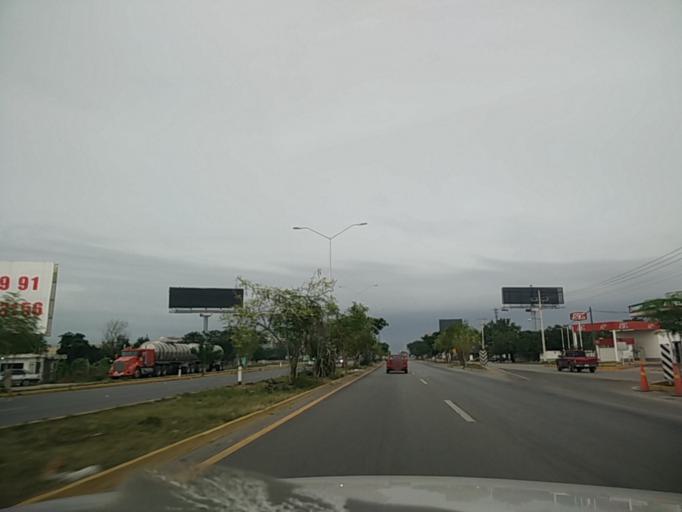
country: MX
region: Yucatan
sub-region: Kanasin
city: Kanasin
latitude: 20.9540
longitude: -89.5647
